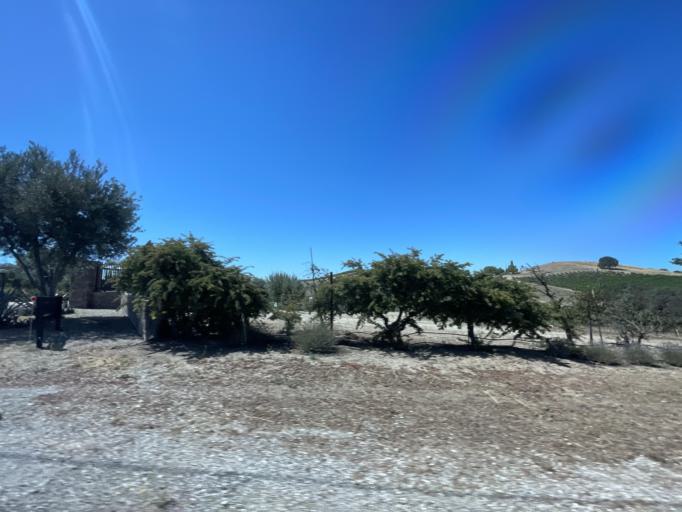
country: US
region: California
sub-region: San Luis Obispo County
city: Paso Robles
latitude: 35.6375
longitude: -120.5942
